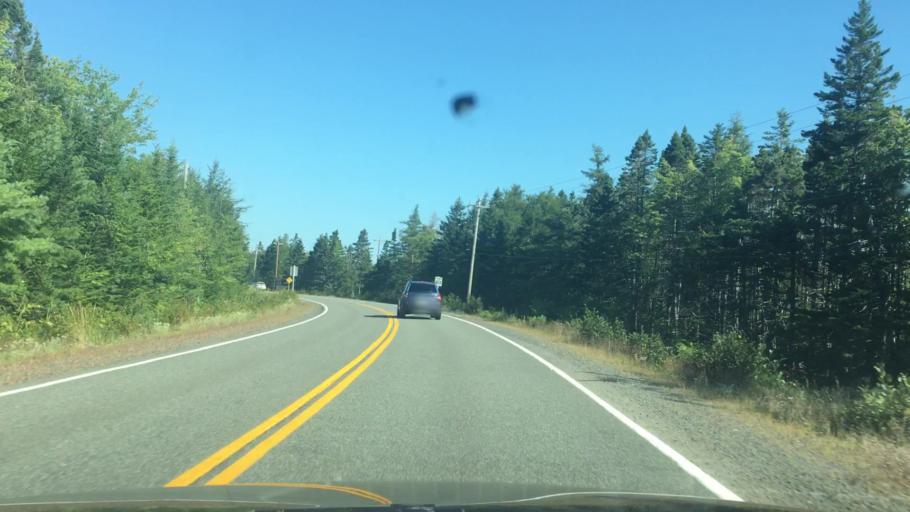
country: CA
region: Nova Scotia
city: Cole Harbour
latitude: 44.8020
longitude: -62.8804
